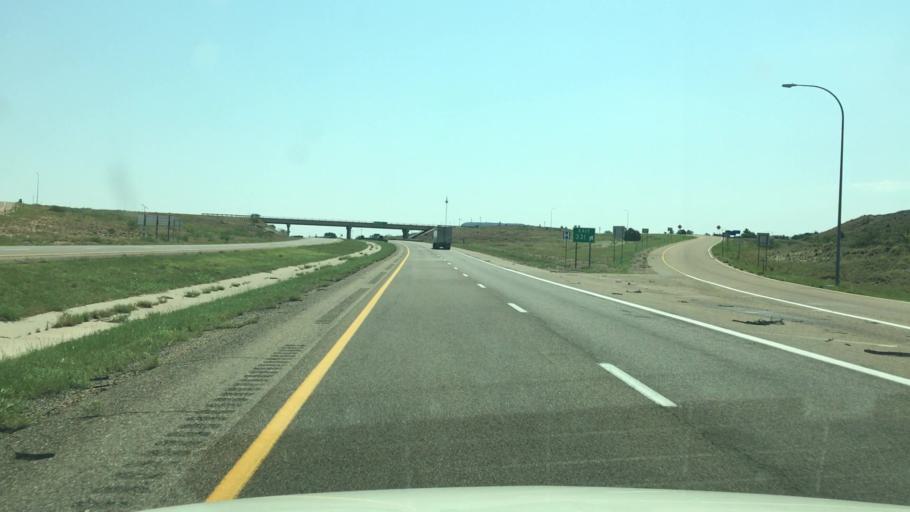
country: US
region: New Mexico
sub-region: Quay County
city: Tucumcari
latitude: 35.1530
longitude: -103.7495
